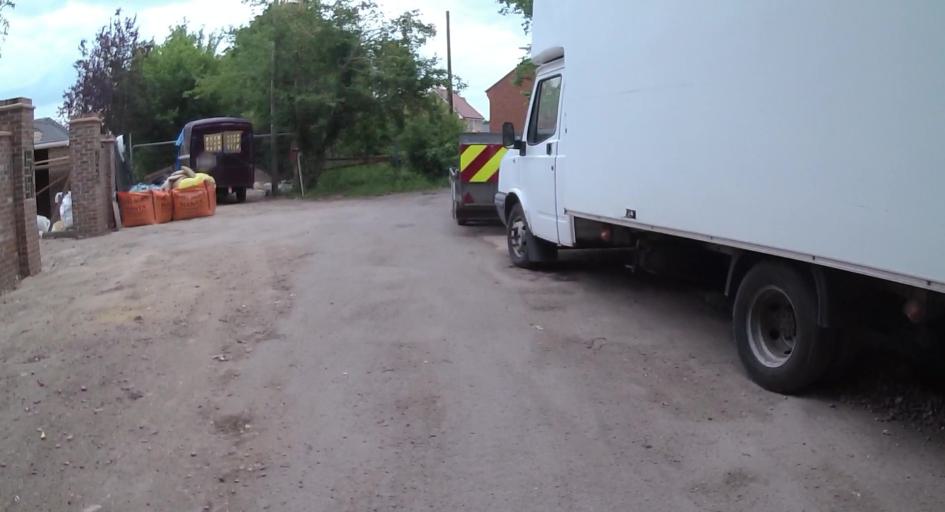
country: GB
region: England
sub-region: Surrey
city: Seale
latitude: 51.2372
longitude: -0.7268
